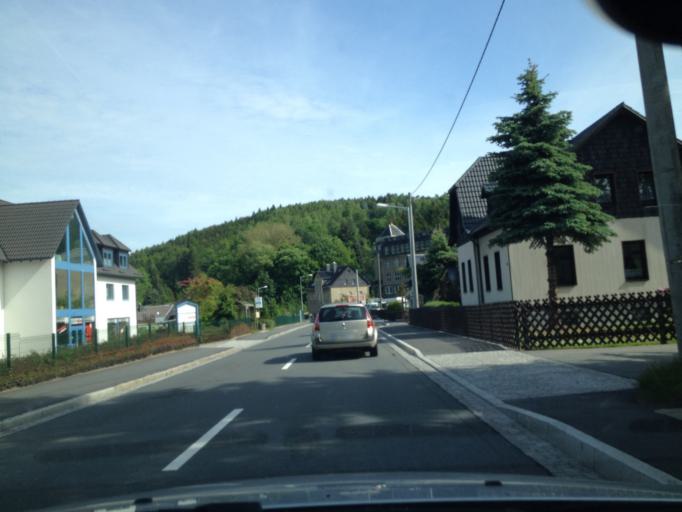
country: DE
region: Saxony
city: Ehrenfriedersdorf
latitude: 50.6546
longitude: 12.9714
